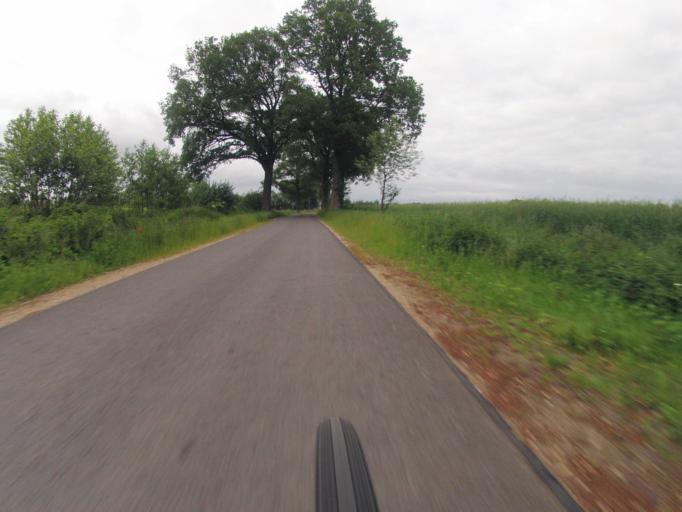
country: DE
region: North Rhine-Westphalia
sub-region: Regierungsbezirk Munster
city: Horstel
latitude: 52.2626
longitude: 7.5722
